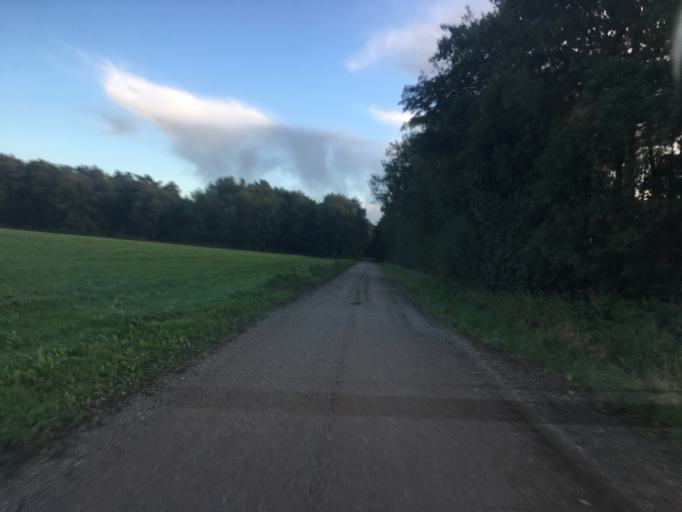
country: DE
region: Schleswig-Holstein
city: Ellhoft
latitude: 54.9482
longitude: 9.0143
